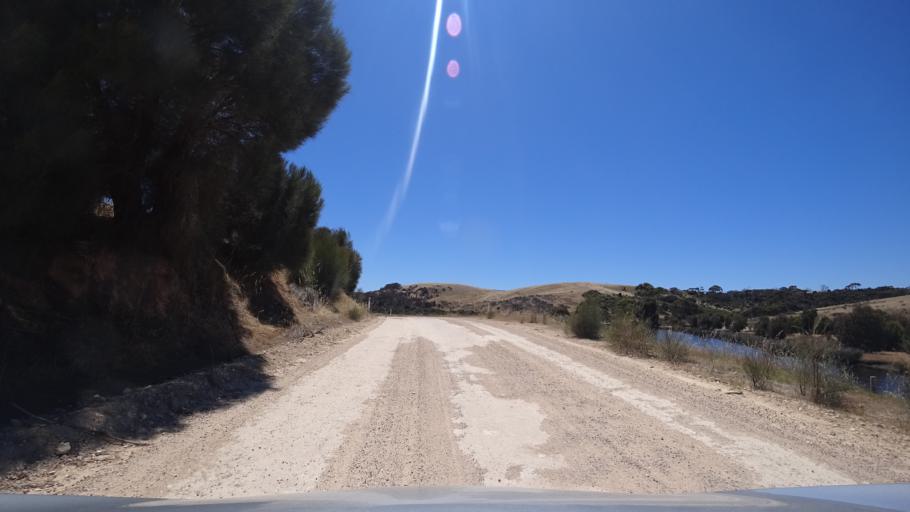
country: AU
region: South Australia
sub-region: Kangaroo Island
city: Kingscote
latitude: -35.6716
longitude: 137.0830
